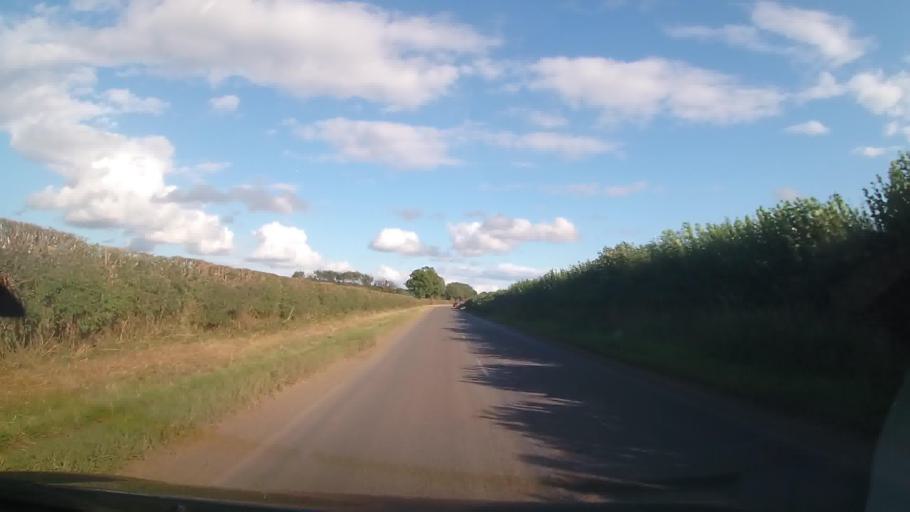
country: GB
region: England
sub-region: Shropshire
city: Great Hanwood
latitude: 52.6593
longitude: -2.8142
